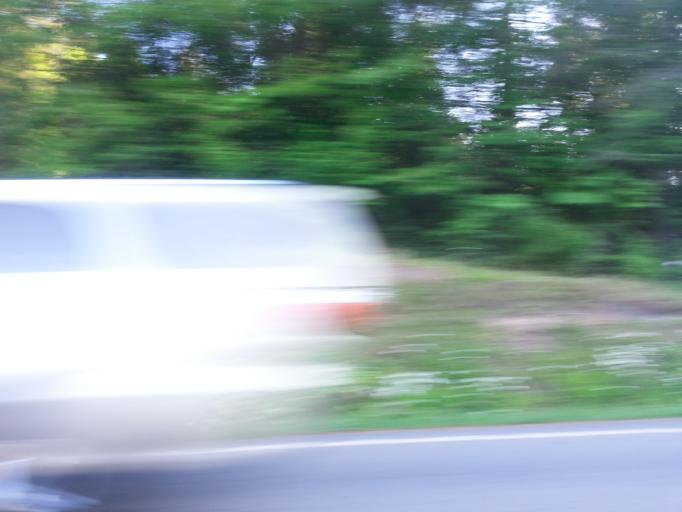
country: US
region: North Carolina
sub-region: Cherokee County
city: Murphy
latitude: 35.0383
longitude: -84.1444
